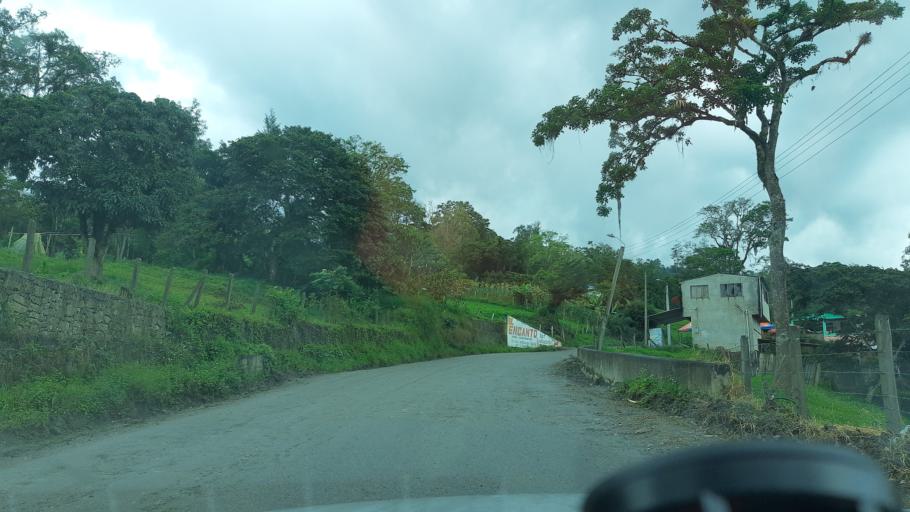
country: CO
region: Boyaca
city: Chinavita
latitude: 5.1305
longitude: -73.3640
